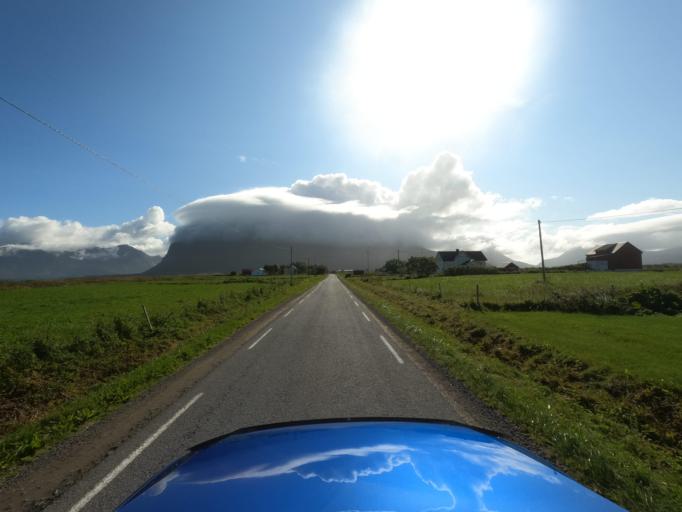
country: NO
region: Nordland
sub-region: Vagan
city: Kabelvag
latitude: 68.3322
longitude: 14.1692
